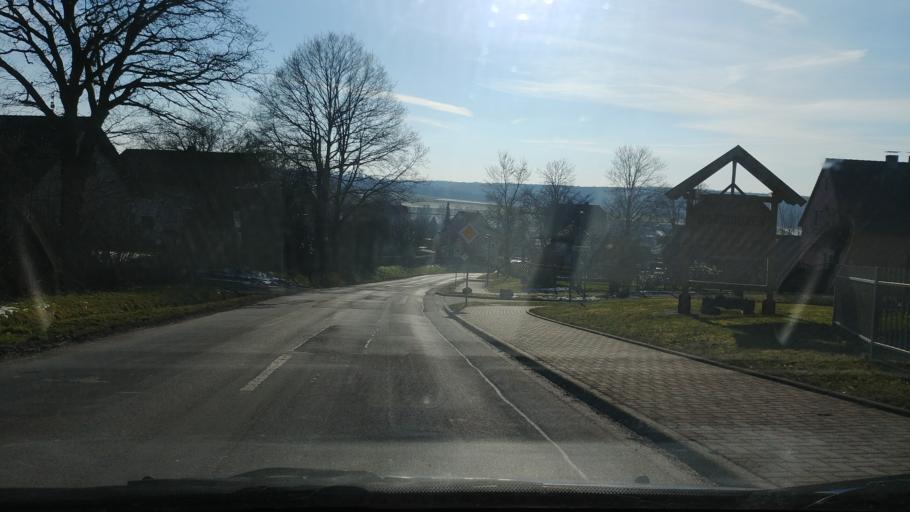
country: DE
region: Lower Saxony
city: Bodenfelde
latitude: 51.5818
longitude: 9.5053
